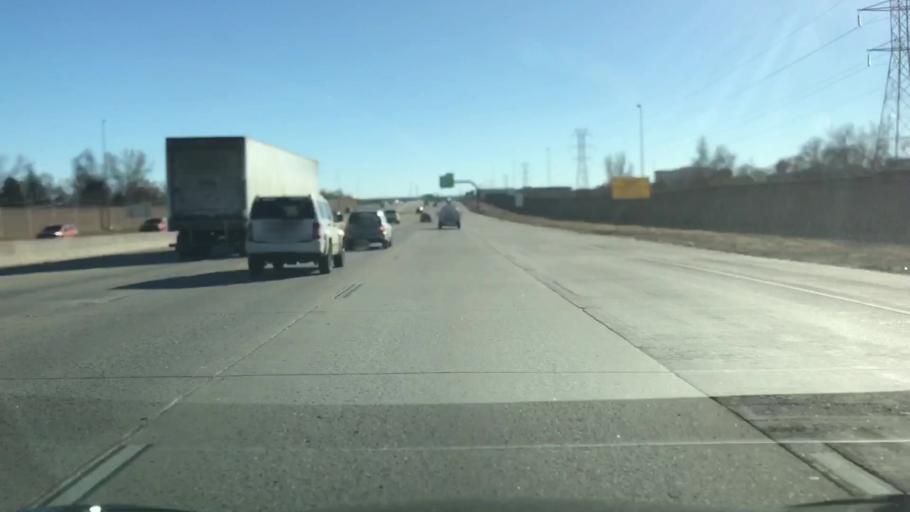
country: US
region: Colorado
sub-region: Adams County
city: Aurora
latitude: 39.7615
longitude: -104.8280
